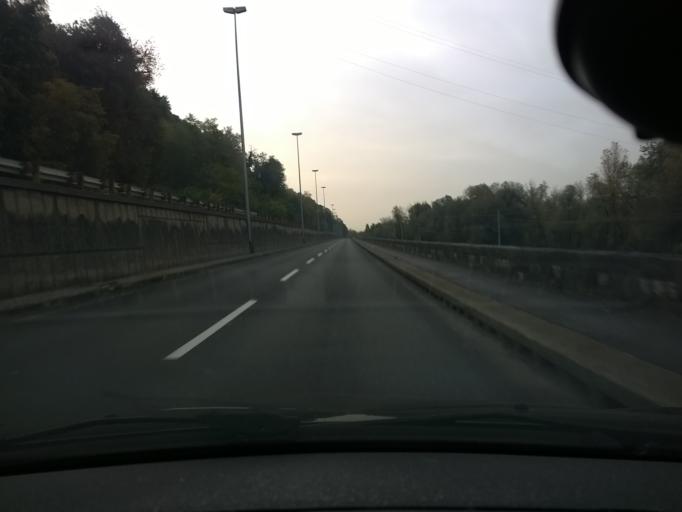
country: HR
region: Zagrebacka
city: Bestovje
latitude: 45.8271
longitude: 15.8259
